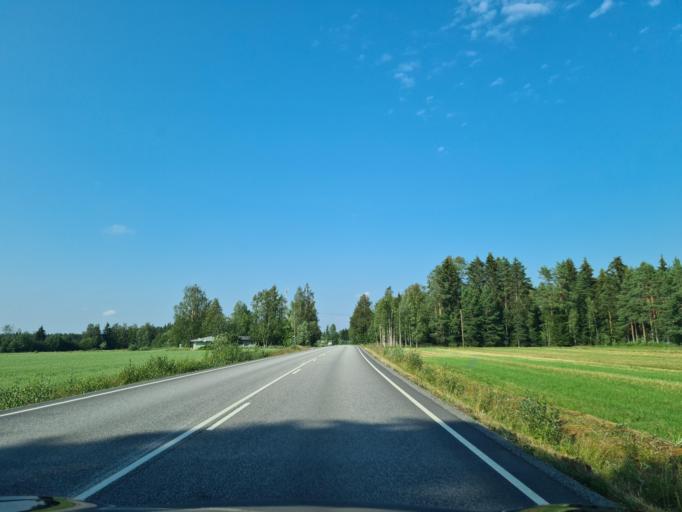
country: FI
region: Satakunta
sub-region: Pohjois-Satakunta
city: Kankaanpaeae
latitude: 61.9377
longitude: 22.5080
